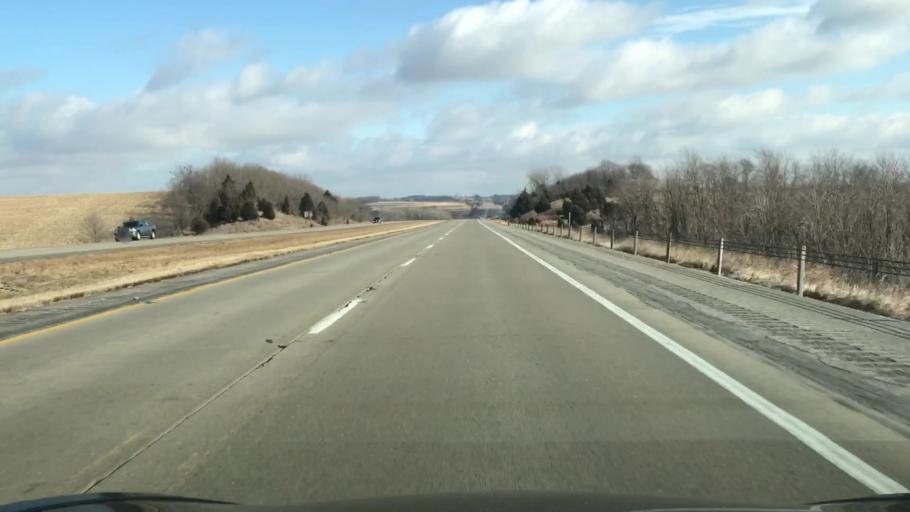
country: US
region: Iowa
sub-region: Cass County
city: Atlantic
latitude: 41.4974
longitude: -94.8781
